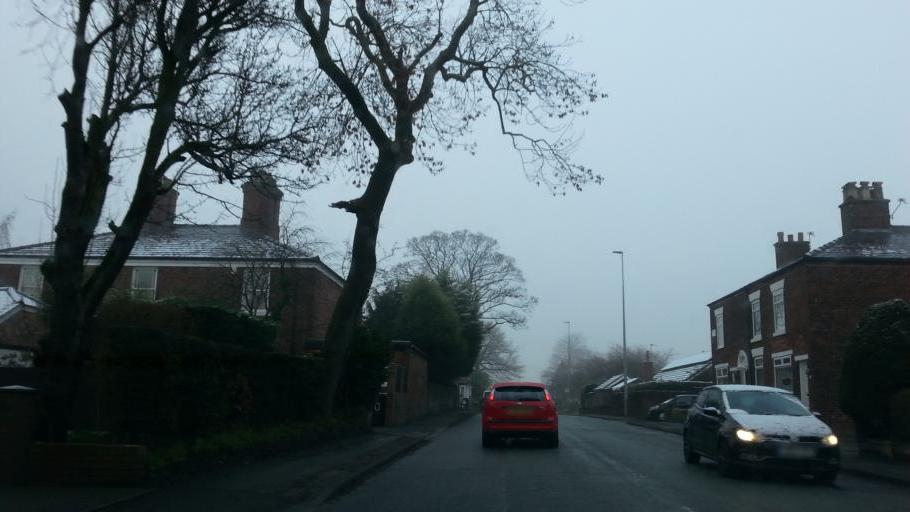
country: GB
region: England
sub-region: Cheshire East
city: Congleton
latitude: 53.1558
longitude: -2.1891
